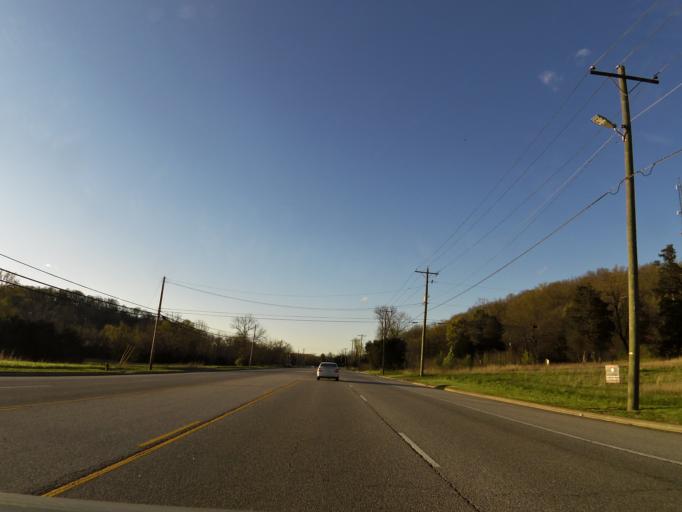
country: US
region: Tennessee
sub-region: Sumner County
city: Millersville
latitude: 36.3536
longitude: -86.7233
